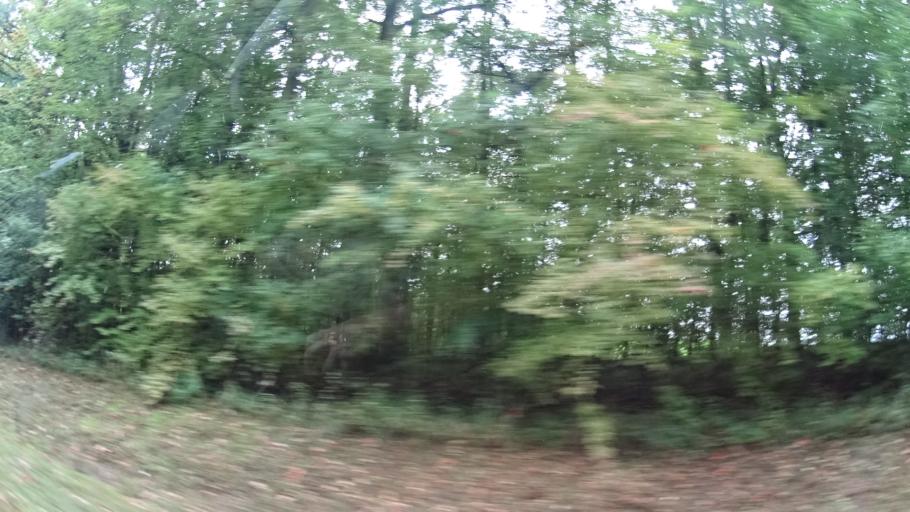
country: DE
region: Bavaria
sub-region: Upper Franconia
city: Schesslitz
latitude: 50.0161
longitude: 11.0105
